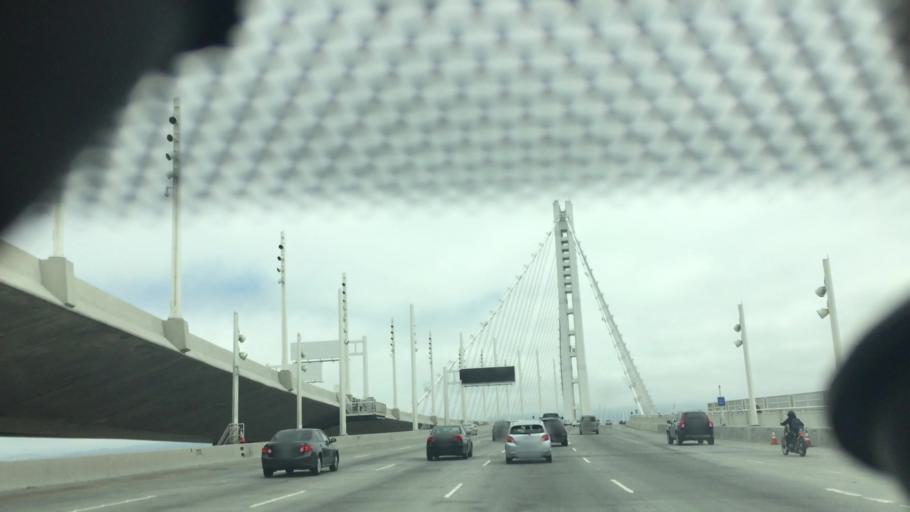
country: US
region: California
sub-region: San Francisco County
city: San Francisco
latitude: 37.8125
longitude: -122.3615
